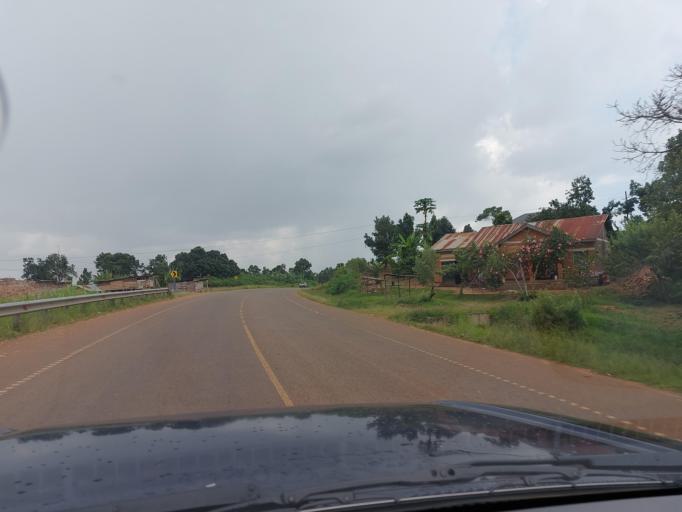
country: UG
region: Central Region
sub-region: Buikwe District
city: Buikwe
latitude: 0.2409
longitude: 32.9303
